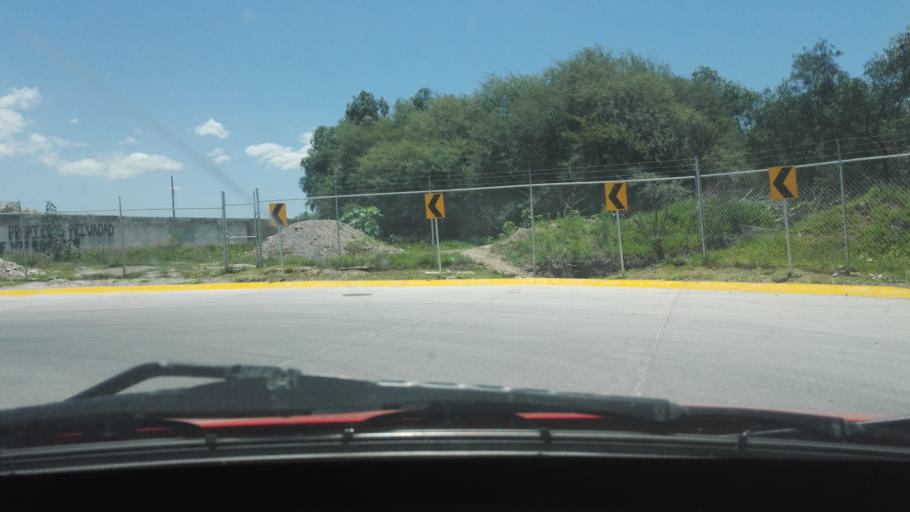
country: MX
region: Guanajuato
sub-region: Leon
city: Ladrilleras del Refugio
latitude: 21.0582
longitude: -101.5653
